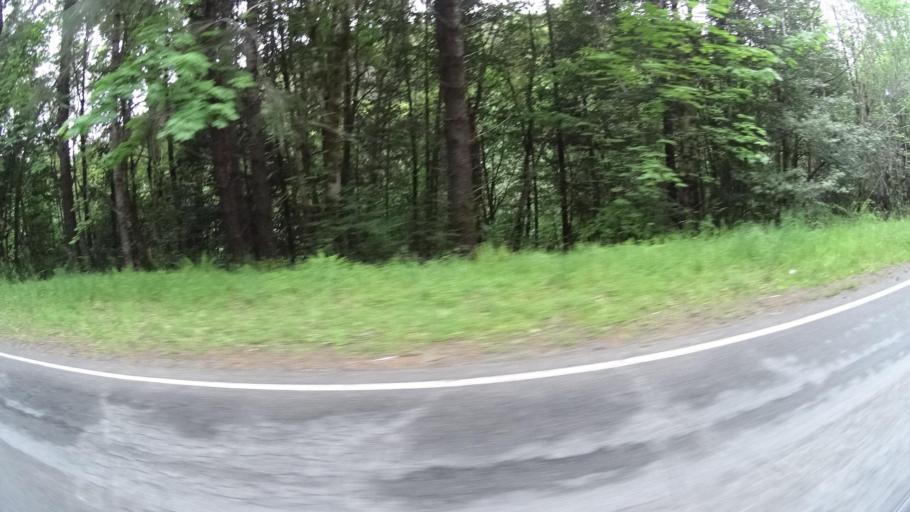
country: US
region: California
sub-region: Humboldt County
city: Willow Creek
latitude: 41.2032
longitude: -123.7518
